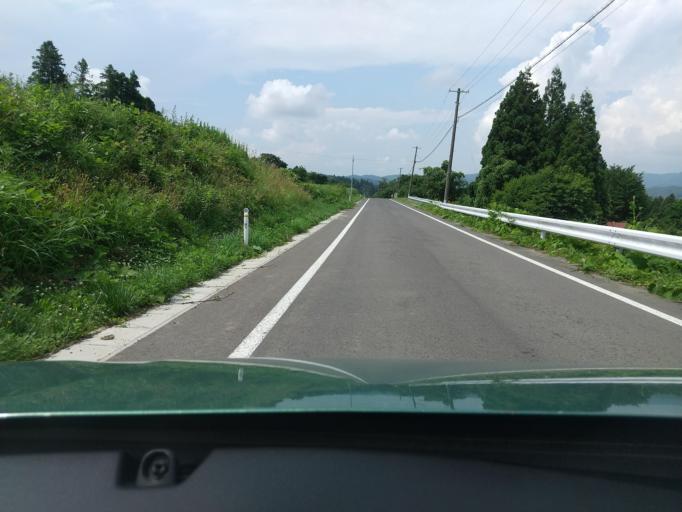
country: JP
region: Iwate
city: Ichinoseki
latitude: 38.9994
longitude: 141.2184
